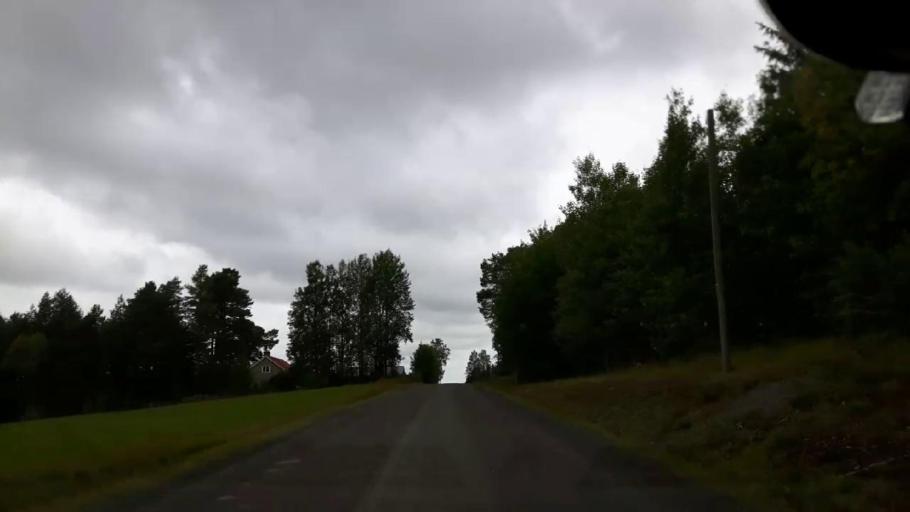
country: SE
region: Jaemtland
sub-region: OEstersunds Kommun
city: Ostersund
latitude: 63.0199
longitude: 14.5865
